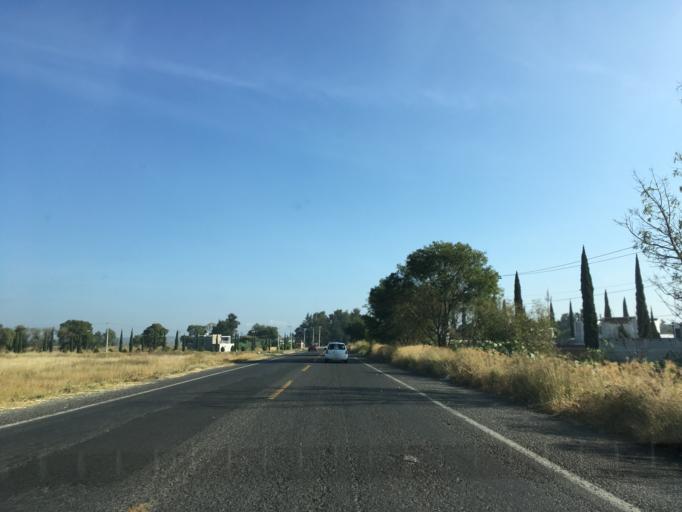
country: MX
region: Michoacan
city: Alvaro Obregon
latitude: 19.8241
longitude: -101.0457
